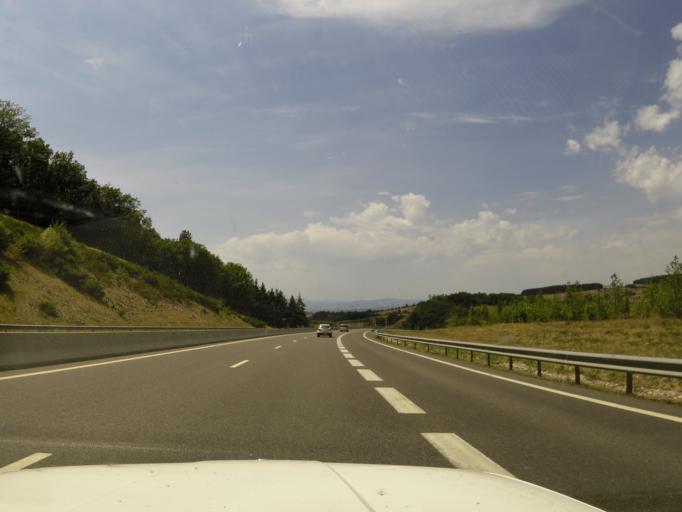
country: FR
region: Rhone-Alpes
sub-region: Departement de la Loire
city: Bussieres
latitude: 45.8694
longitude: 4.2818
